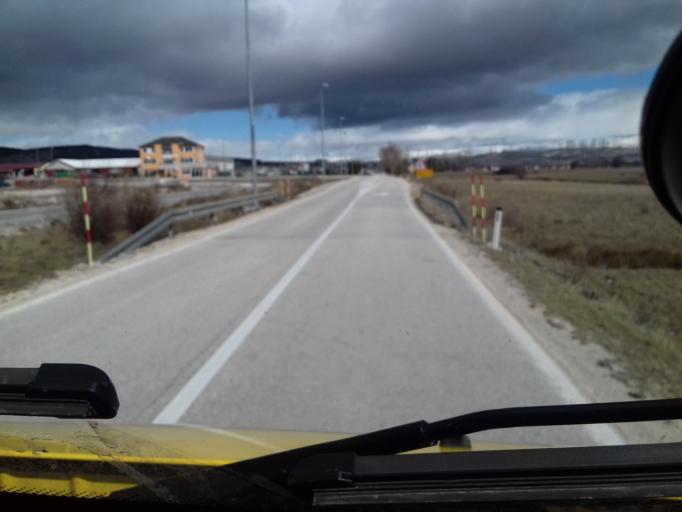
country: BA
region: Federation of Bosnia and Herzegovina
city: Tomislavgrad
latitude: 43.6795
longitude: 17.2016
